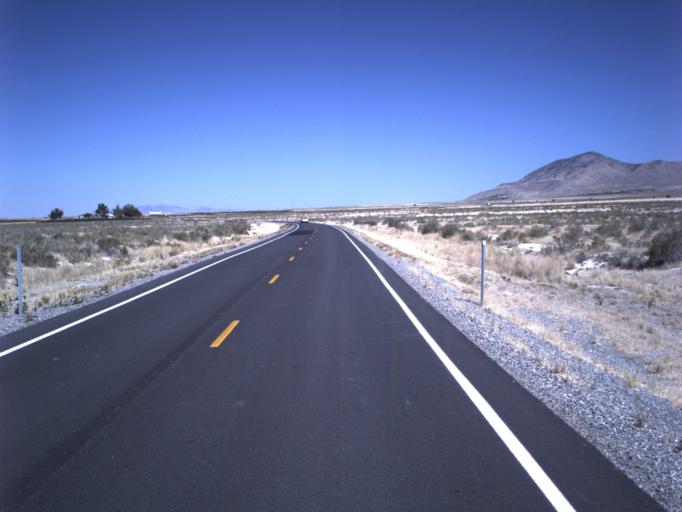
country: US
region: Utah
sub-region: Tooele County
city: Grantsville
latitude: 40.4801
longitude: -112.7455
